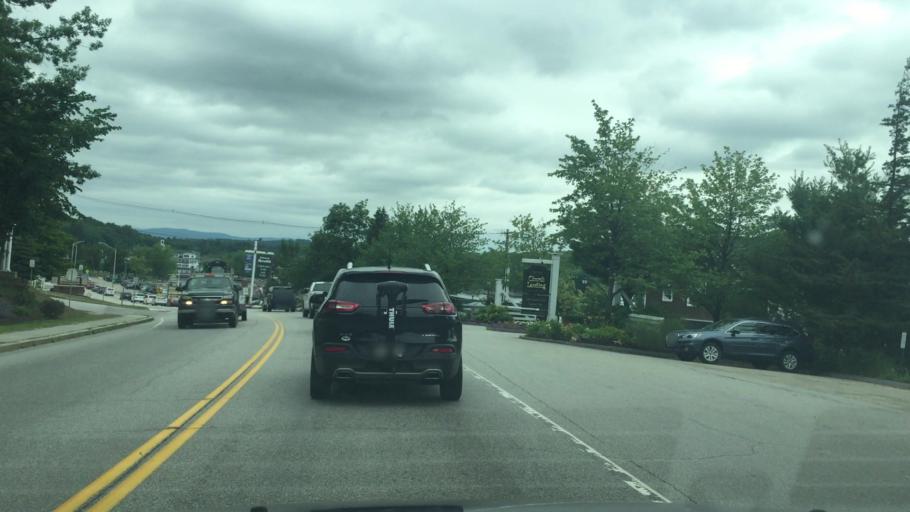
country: US
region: New Hampshire
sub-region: Belknap County
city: Meredith
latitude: 43.6535
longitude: -71.4968
